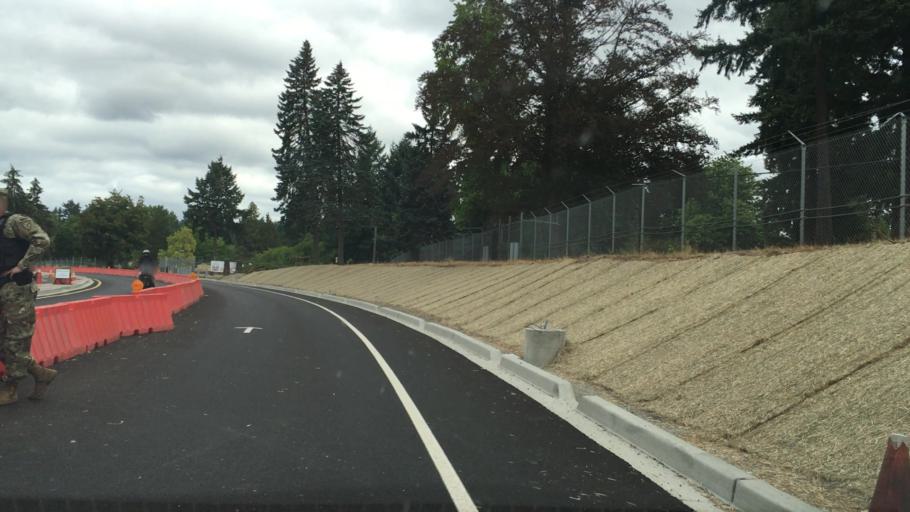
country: US
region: Washington
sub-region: Pierce County
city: Fort Lewis
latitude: 47.1006
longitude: -122.5864
